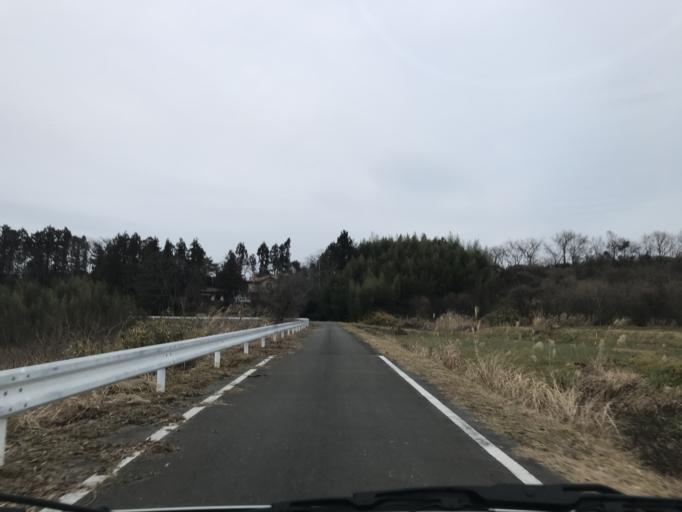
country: JP
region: Miyagi
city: Wakuya
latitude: 38.6992
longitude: 141.1522
